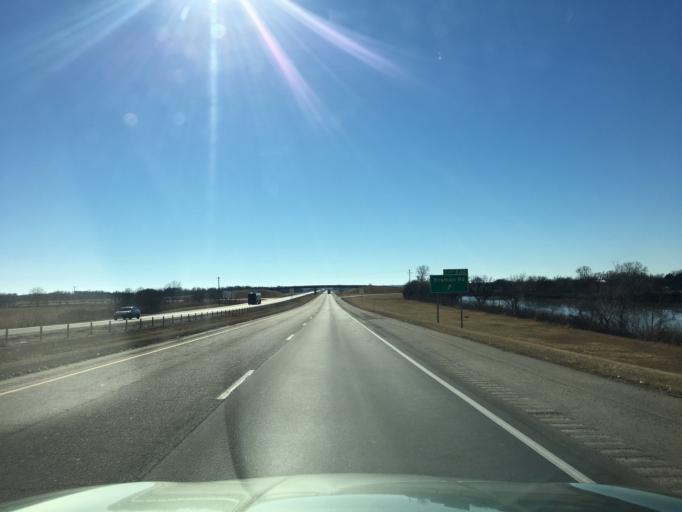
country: US
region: Oklahoma
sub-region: Kay County
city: Blackwell
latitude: 36.9319
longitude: -97.3484
